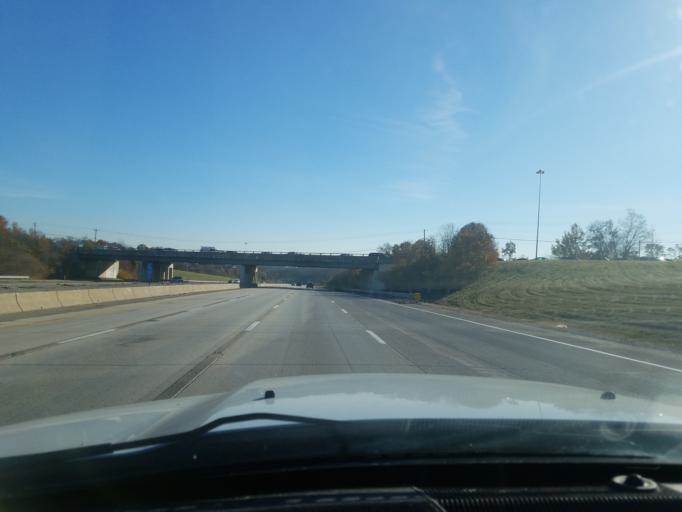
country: US
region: Kentucky
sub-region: Kenton County
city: Lakeside Park
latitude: 39.0263
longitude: -84.5711
